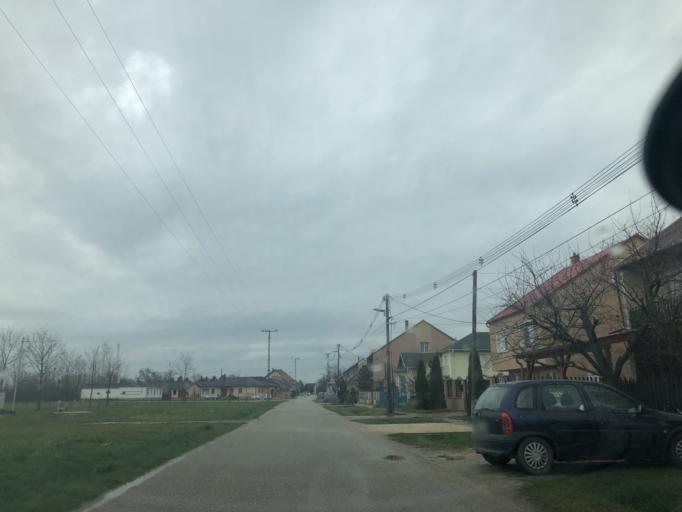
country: HU
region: Gyor-Moson-Sopron
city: Kapuvar
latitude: 47.5856
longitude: 17.0167
